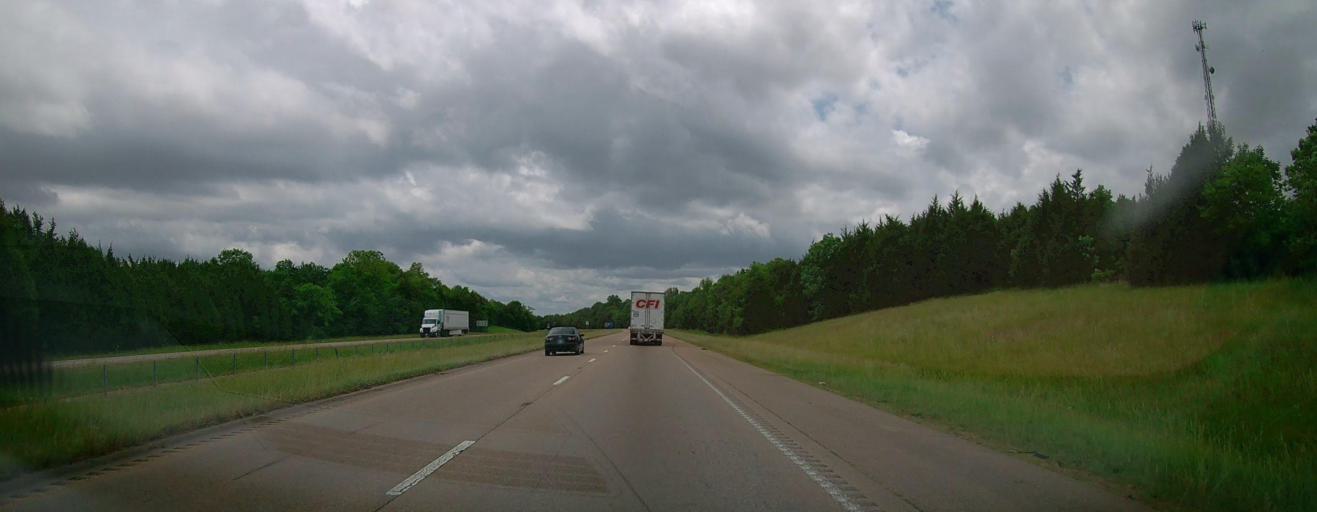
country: US
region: Mississippi
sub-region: Lee County
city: Tupelo
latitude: 34.3197
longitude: -88.8075
